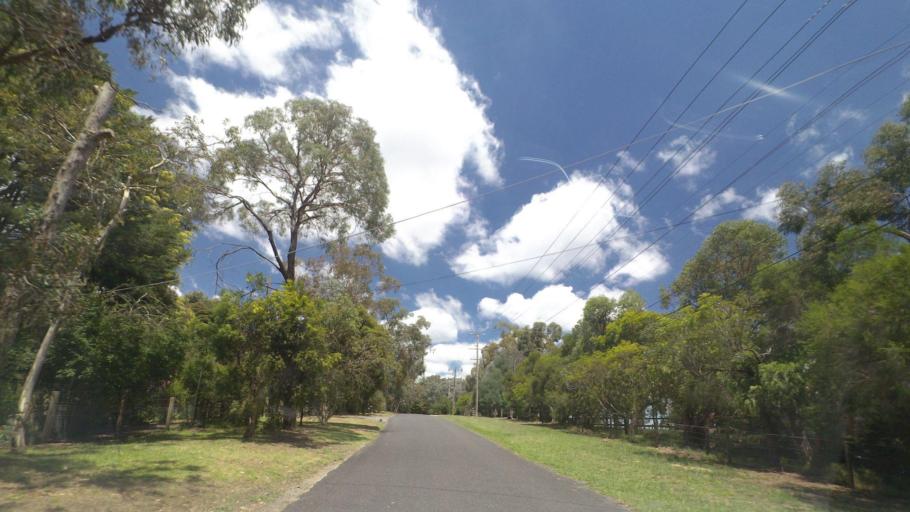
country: AU
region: Victoria
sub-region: Manningham
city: Warrandyte
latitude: -37.7404
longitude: 145.2566
